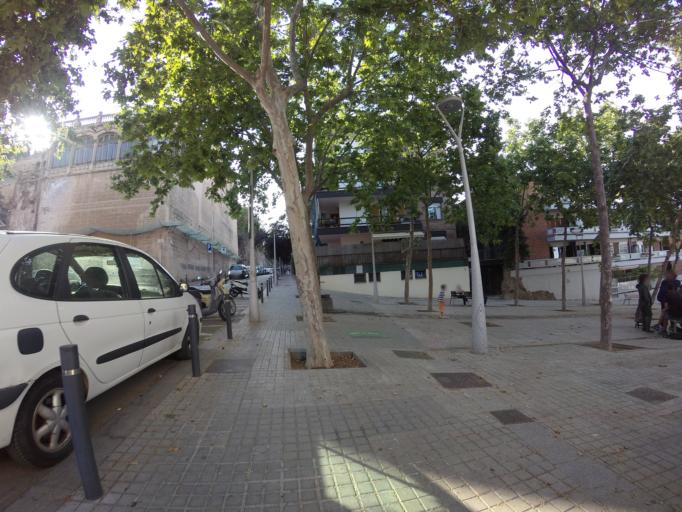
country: ES
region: Catalonia
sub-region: Provincia de Barcelona
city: Gracia
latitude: 41.4115
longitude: 2.1531
